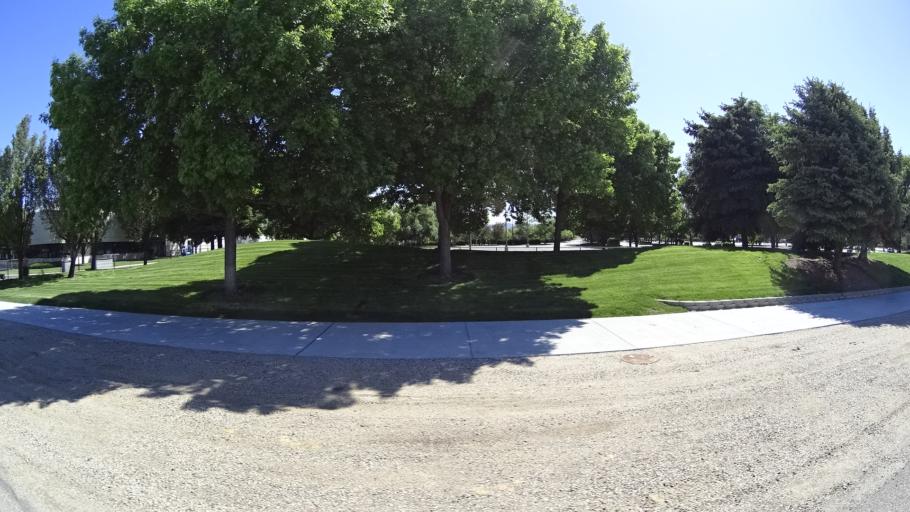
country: US
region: Idaho
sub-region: Ada County
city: Boise
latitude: 43.5321
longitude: -116.1517
